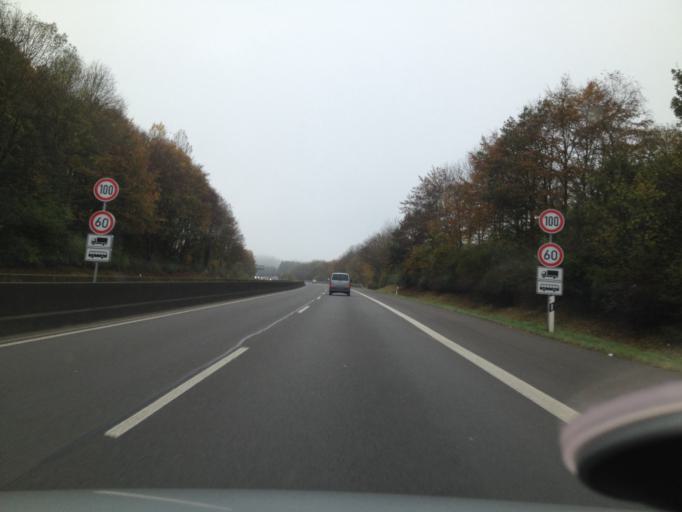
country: DE
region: North Rhine-Westphalia
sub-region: Regierungsbezirk Arnsberg
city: Drolshagen
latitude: 50.9838
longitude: 7.8074
